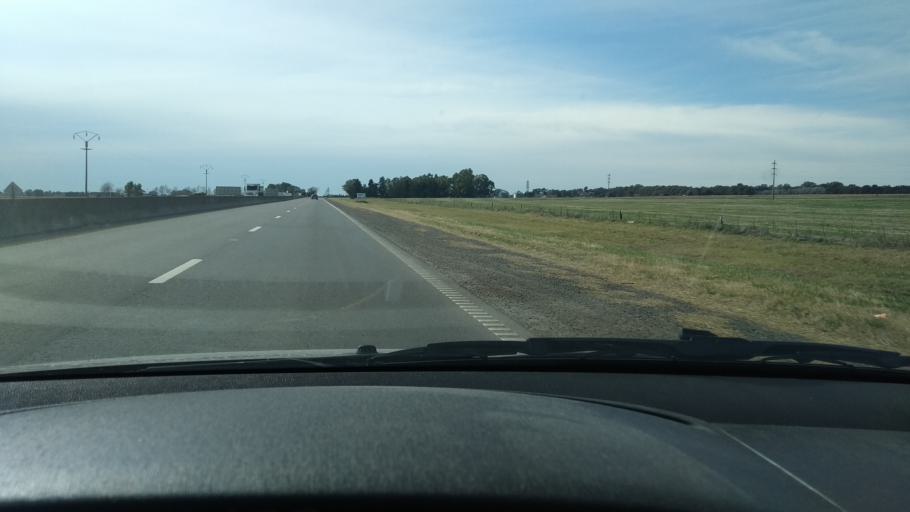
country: AR
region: Buenos Aires
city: Olavarria
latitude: -36.9082
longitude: -60.1941
